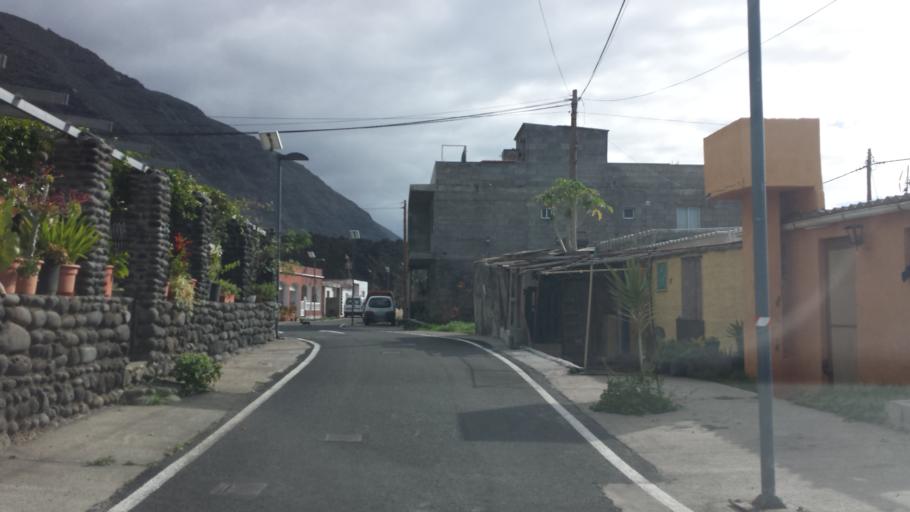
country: ES
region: Canary Islands
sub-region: Provincia de Santa Cruz de Tenerife
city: Fuencaliente de la Palma
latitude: 28.5525
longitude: -17.8882
